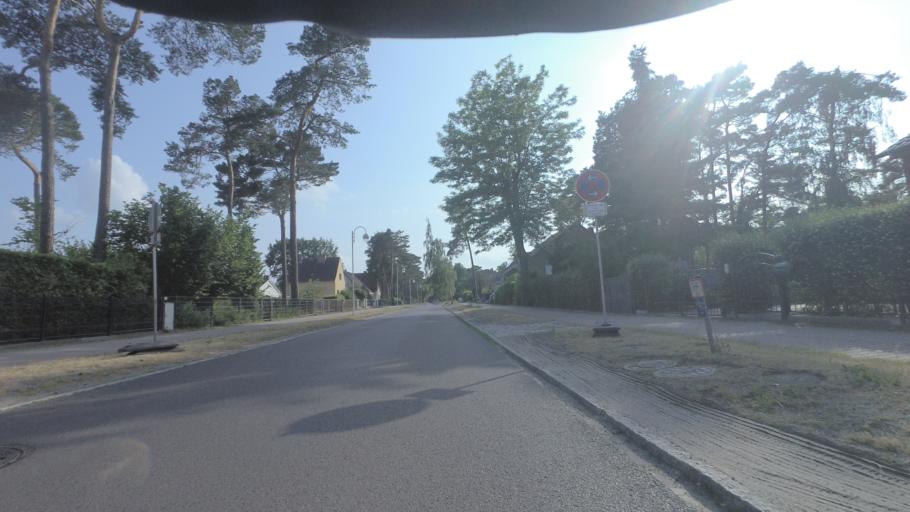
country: DE
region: Brandenburg
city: Rangsdorf
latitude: 52.3432
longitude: 13.4250
